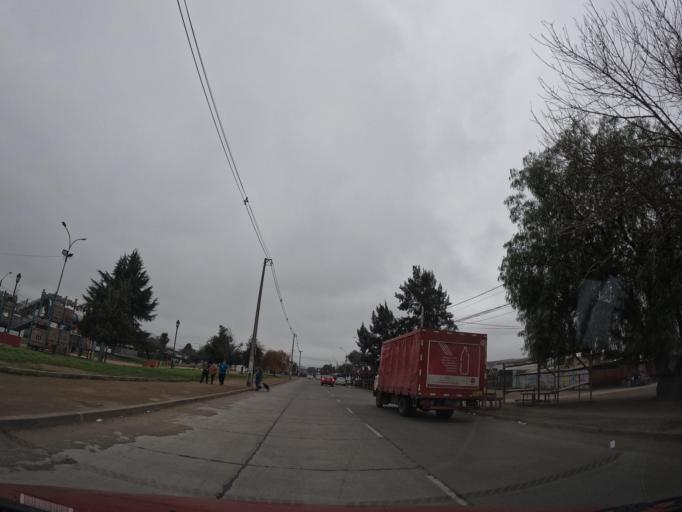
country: CL
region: Maule
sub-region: Provincia de Talca
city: Talca
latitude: -35.4421
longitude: -71.6339
